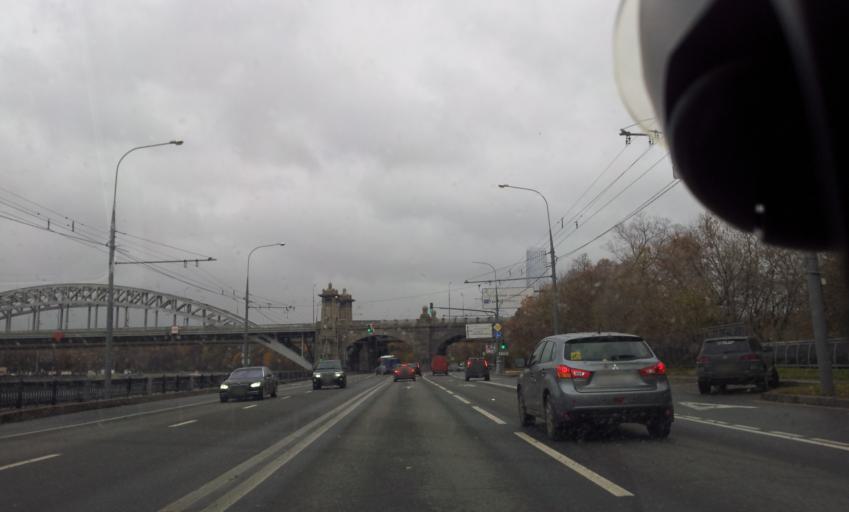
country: RU
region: Moscow
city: Luzhniki
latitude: 55.7300
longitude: 37.5499
